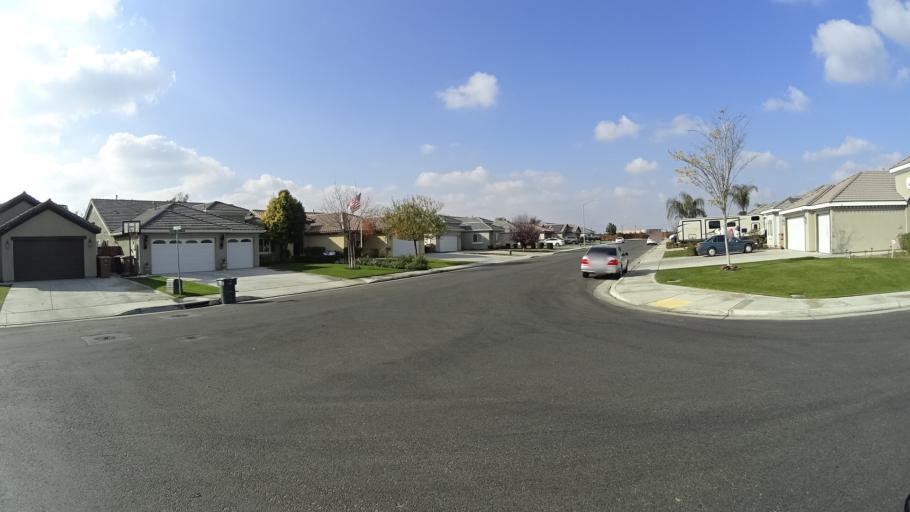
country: US
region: California
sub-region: Kern County
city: Greenacres
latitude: 35.2930
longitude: -119.1062
